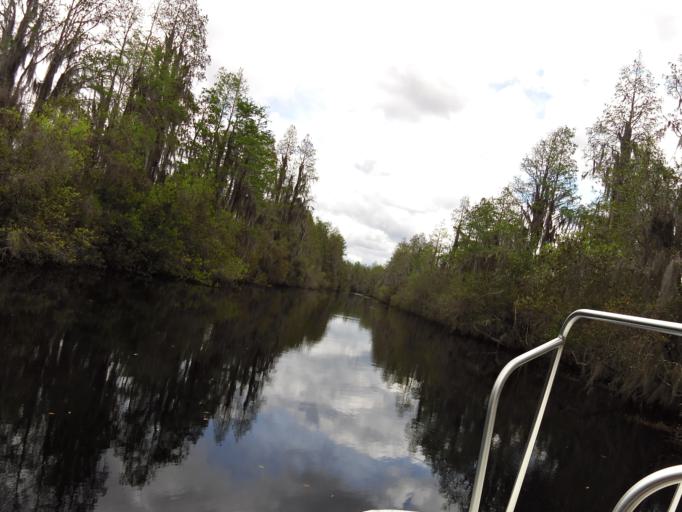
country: US
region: Georgia
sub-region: Charlton County
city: Folkston
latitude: 30.7373
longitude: -82.1736
